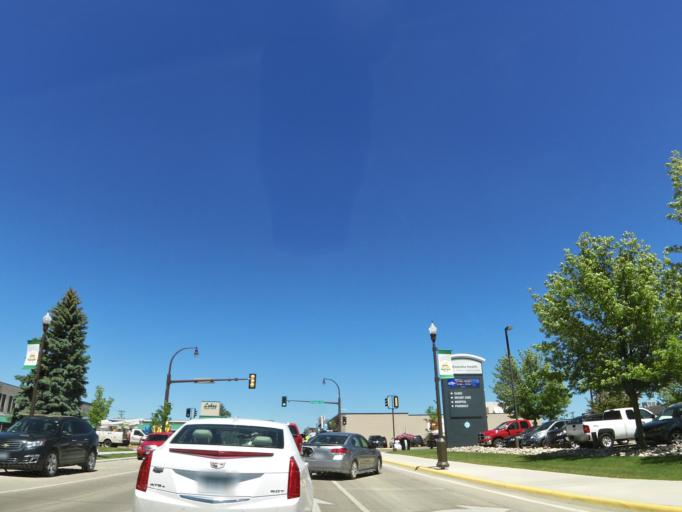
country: US
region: Minnesota
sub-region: Becker County
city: Detroit Lakes
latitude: 46.8154
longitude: -95.8454
